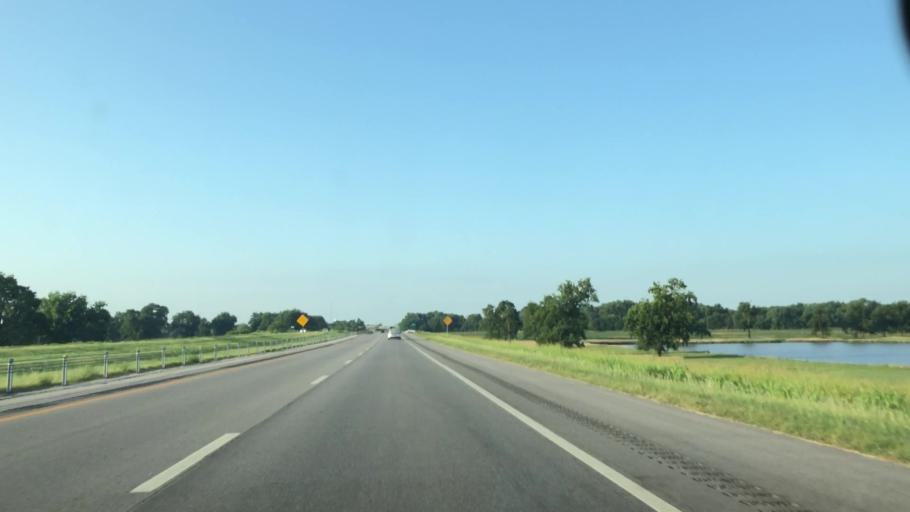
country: US
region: Oklahoma
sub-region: Washington County
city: Bartlesville
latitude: 36.6525
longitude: -95.9356
